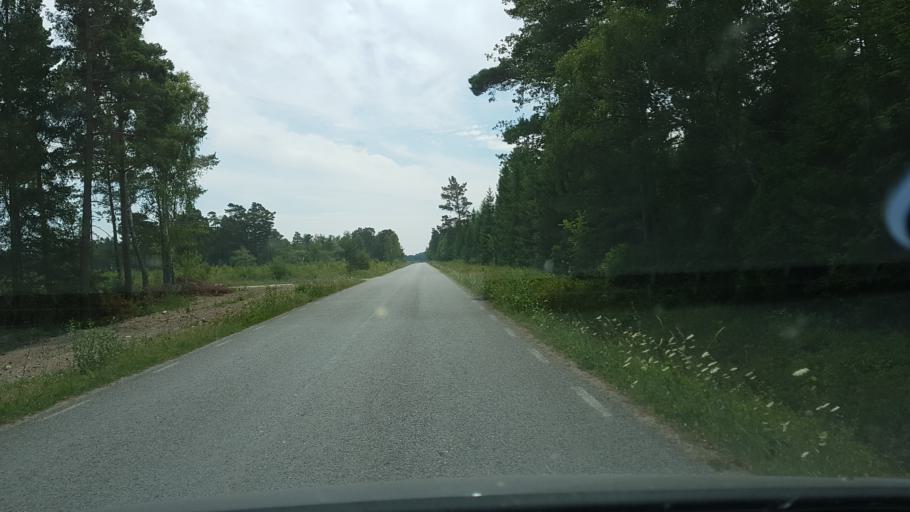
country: SE
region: Gotland
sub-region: Gotland
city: Visby
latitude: 57.7132
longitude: 18.5081
